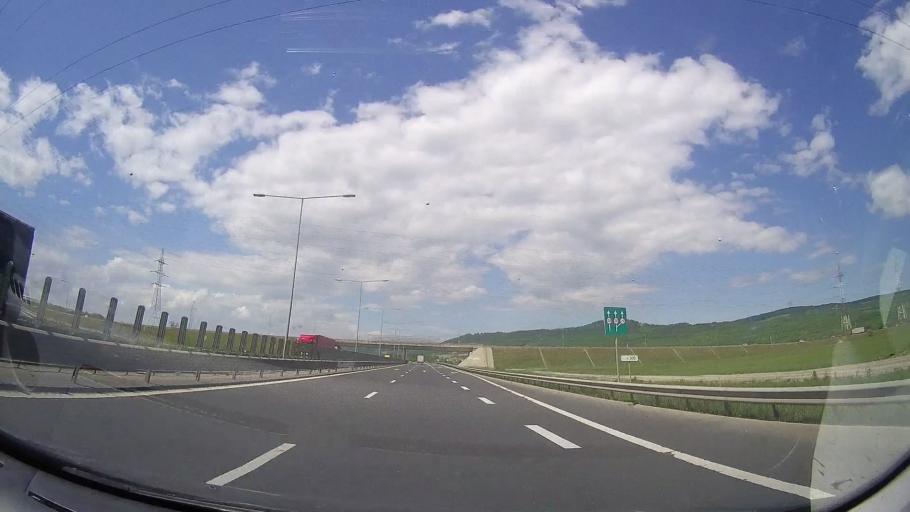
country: RO
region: Sibiu
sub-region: Comuna Selimbar
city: Selimbar
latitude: 45.7878
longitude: 24.1996
